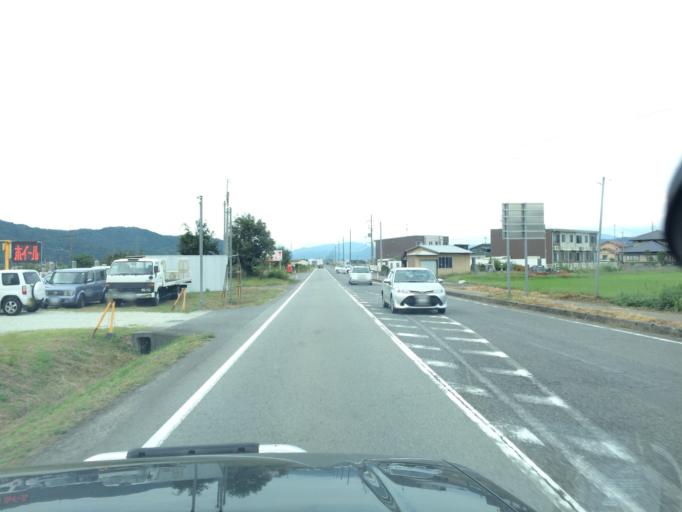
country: JP
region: Hyogo
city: Toyooka
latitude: 35.4827
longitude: 134.7887
